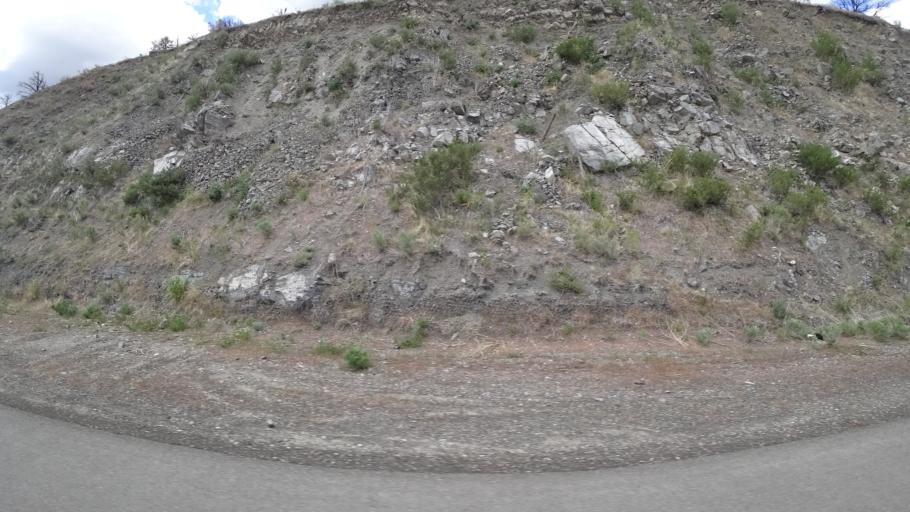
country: US
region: Nevada
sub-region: Lyon County
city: Smith Valley
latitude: 38.6671
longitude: -119.5445
